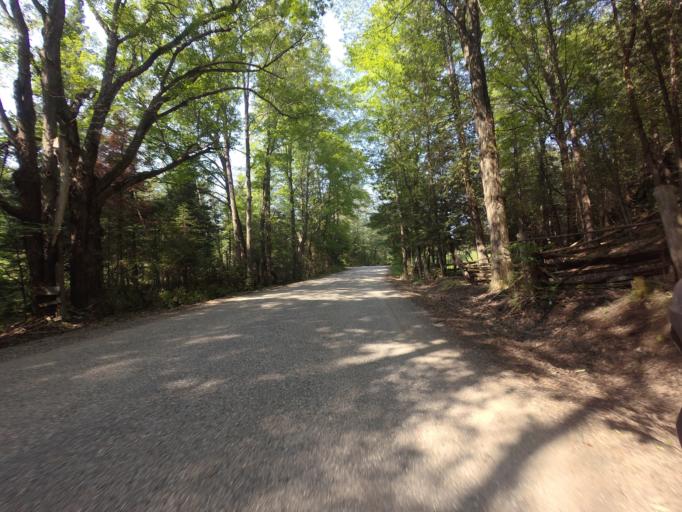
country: CA
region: Ontario
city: Skatepark
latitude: 44.7450
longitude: -76.8288
